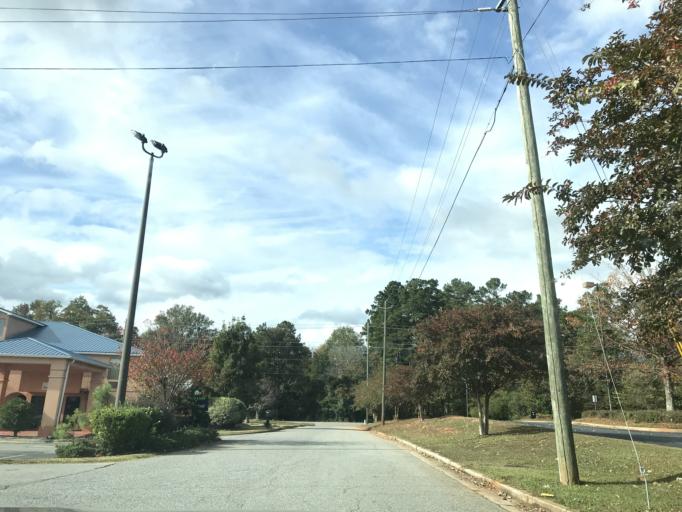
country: US
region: Georgia
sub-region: Jones County
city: Gray
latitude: 33.0047
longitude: -83.5488
